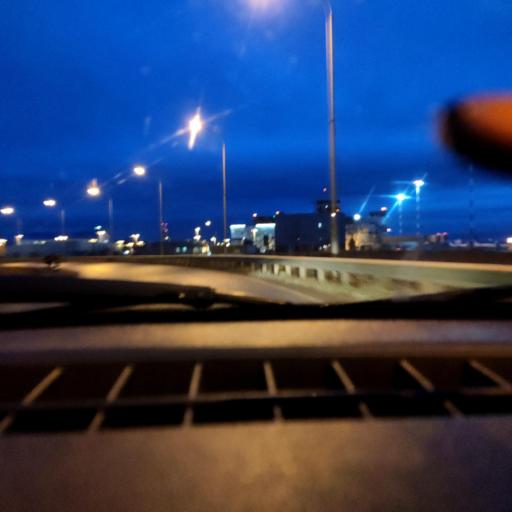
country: RU
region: Bashkortostan
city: Avdon
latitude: 54.5688
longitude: 55.8804
